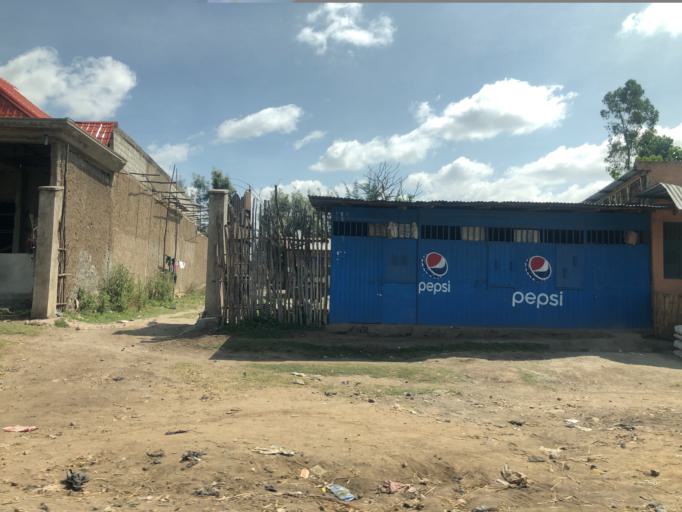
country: ET
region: Oromiya
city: Shashemene
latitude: 7.2224
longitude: 38.6264
